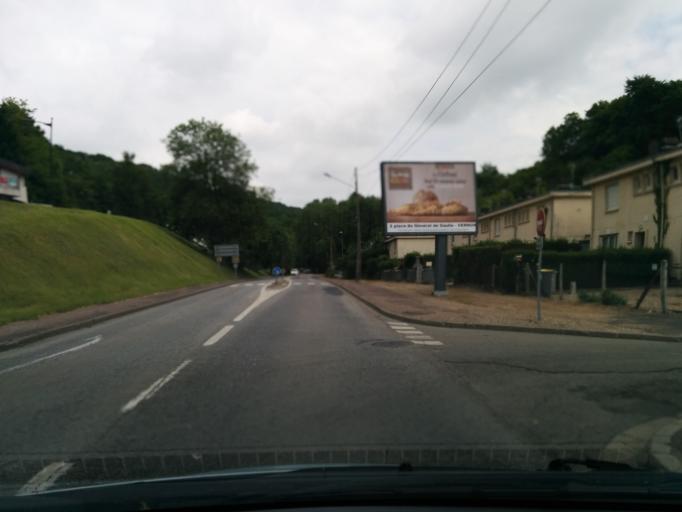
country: FR
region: Haute-Normandie
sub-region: Departement de l'Eure
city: Vernon
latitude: 49.1059
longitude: 1.4871
